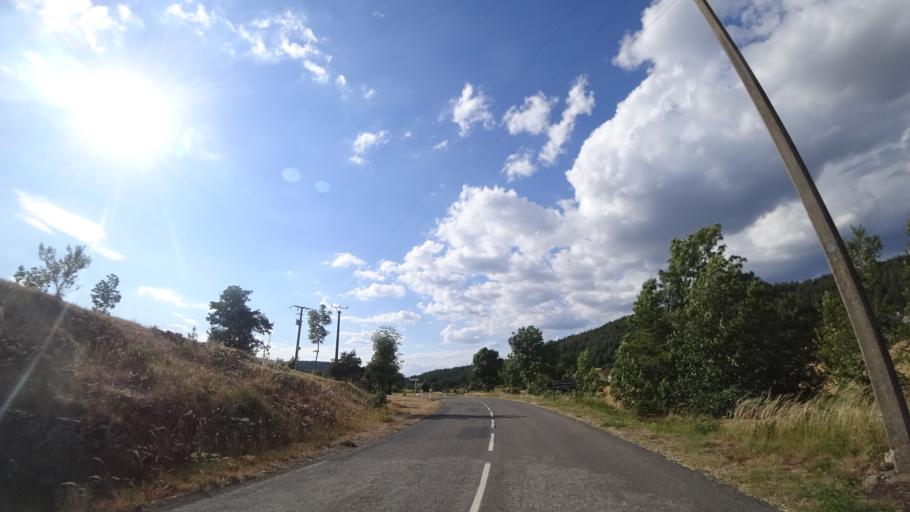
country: FR
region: Languedoc-Roussillon
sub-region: Departement de la Lozere
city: Chanac
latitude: 44.3880
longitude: 3.3039
